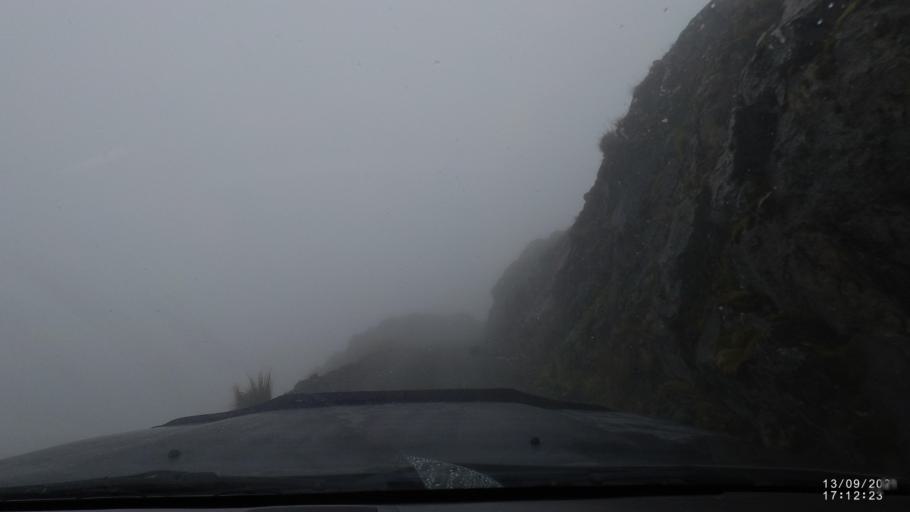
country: BO
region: Cochabamba
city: Colomi
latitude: -17.3385
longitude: -65.7461
